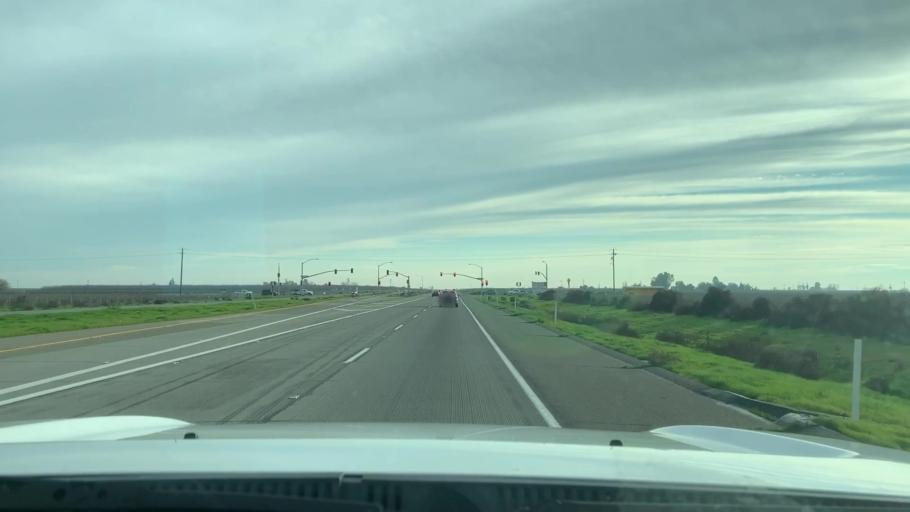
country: US
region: California
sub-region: Fresno County
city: Caruthers
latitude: 36.5494
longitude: -119.7863
